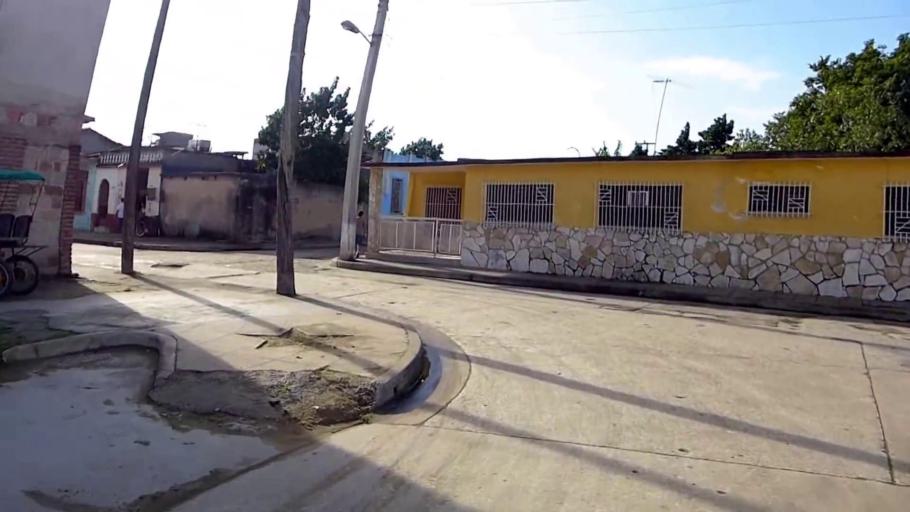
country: CU
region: Camaguey
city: Camaguey
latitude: 21.3847
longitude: -77.9289
